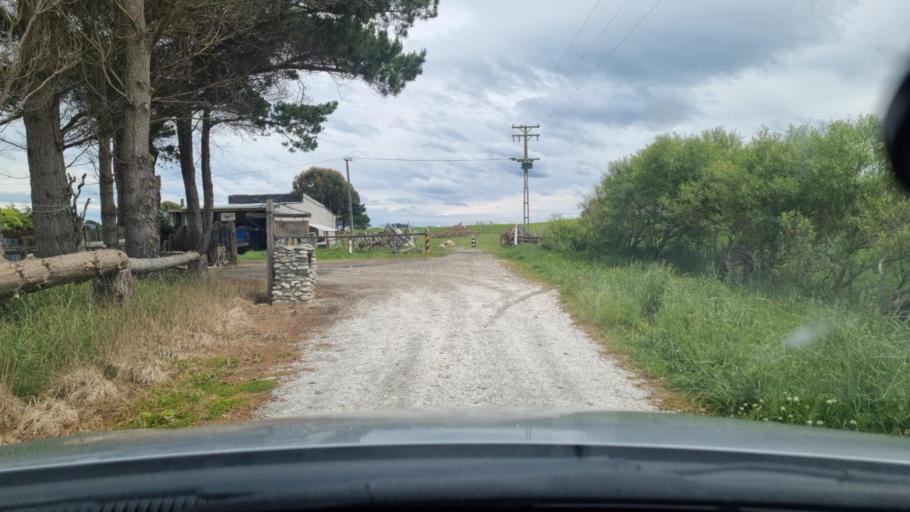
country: NZ
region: Southland
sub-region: Invercargill City
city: Invercargill
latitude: -46.3922
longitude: 168.2919
